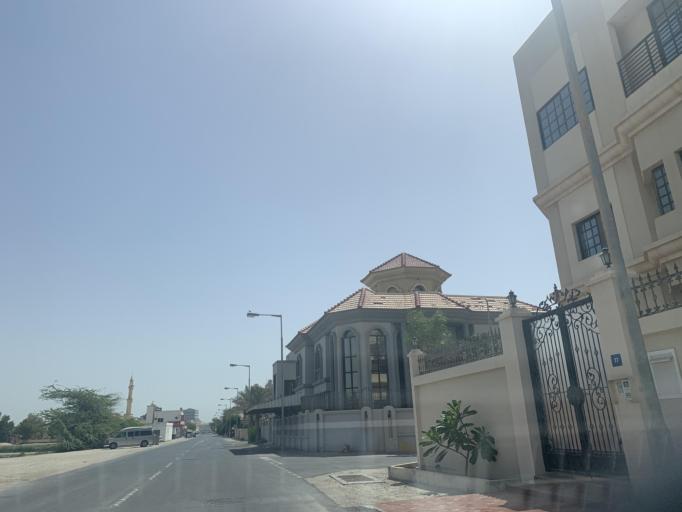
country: BH
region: Manama
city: Jidd Hafs
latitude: 26.2037
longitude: 50.5603
